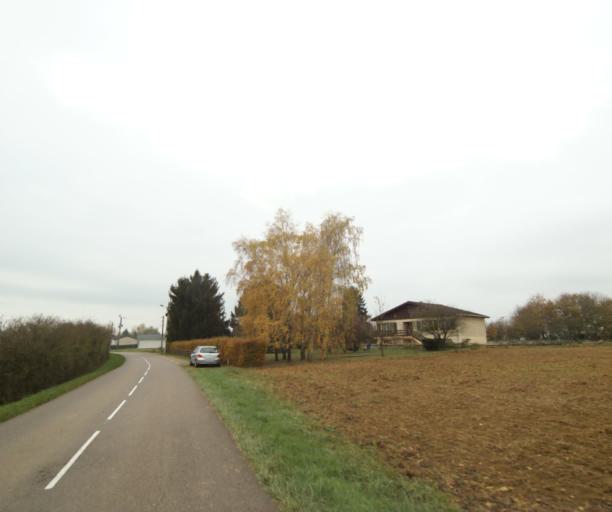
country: FR
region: Lorraine
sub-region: Departement de Meurthe-et-Moselle
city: Mancieulles
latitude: 49.2792
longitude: 5.8806
